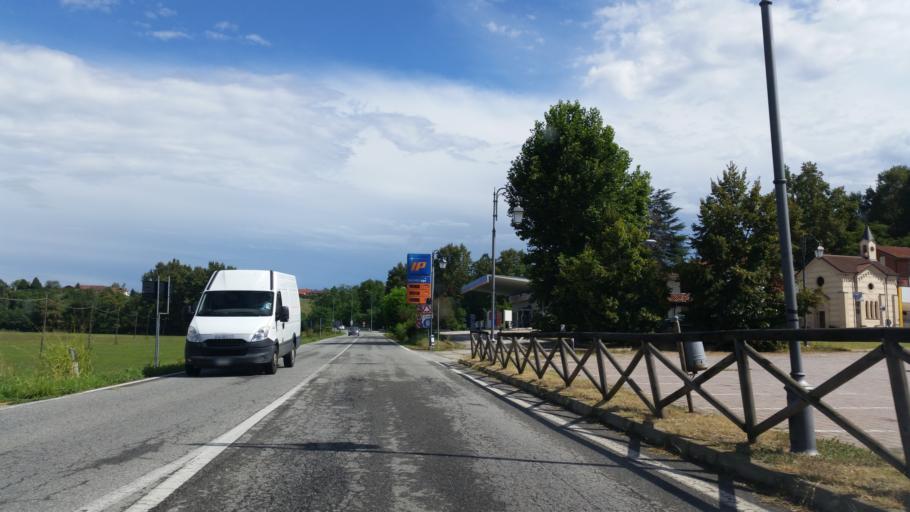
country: IT
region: Piedmont
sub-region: Provincia di Torino
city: Pralormo
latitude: 44.8623
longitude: 7.8961
